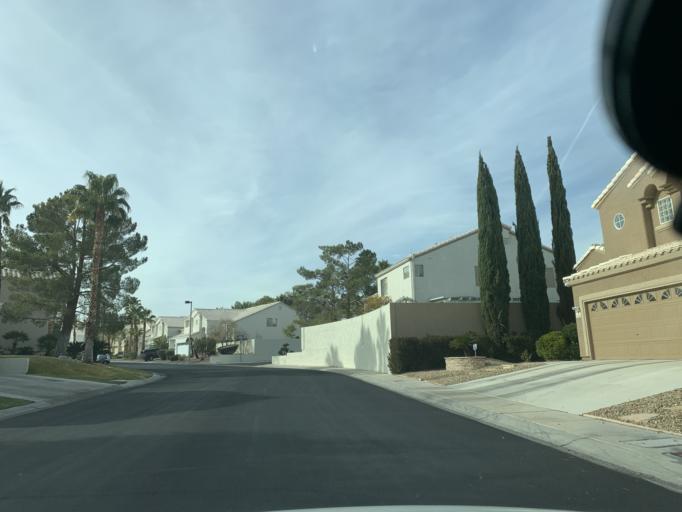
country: US
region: Nevada
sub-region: Clark County
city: Summerlin South
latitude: 36.1549
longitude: -115.2968
